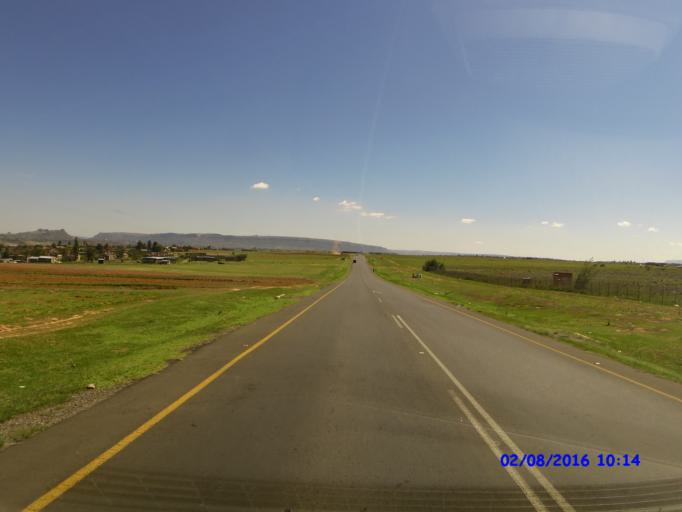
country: LS
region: Maseru
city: Maseru
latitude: -29.4346
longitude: 27.5591
